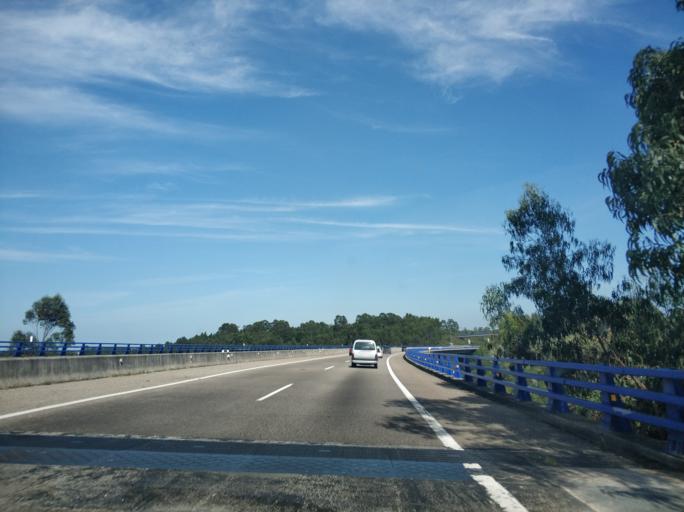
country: ES
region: Asturias
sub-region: Province of Asturias
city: Castrillon
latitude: 43.5486
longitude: -5.9777
